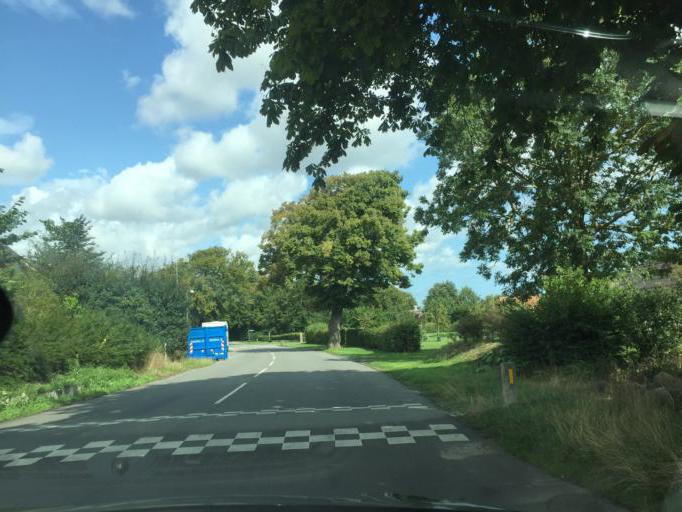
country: DK
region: South Denmark
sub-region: Odense Kommune
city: Stige
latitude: 55.4580
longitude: 10.3779
